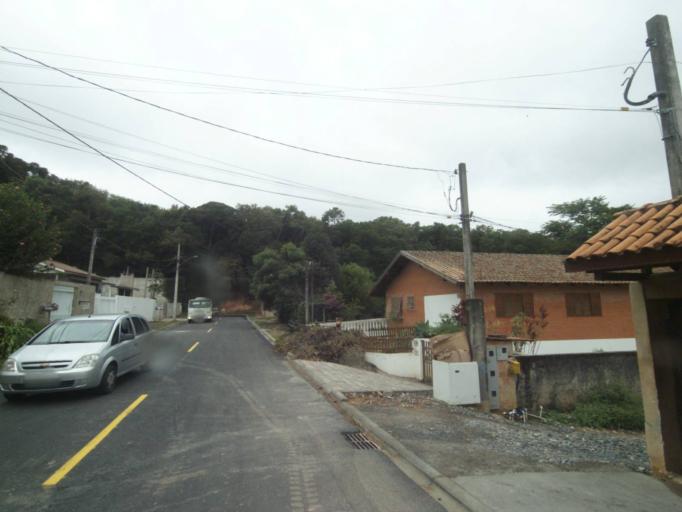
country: BR
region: Parana
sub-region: Curitiba
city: Curitiba
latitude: -25.4225
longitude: -49.3347
